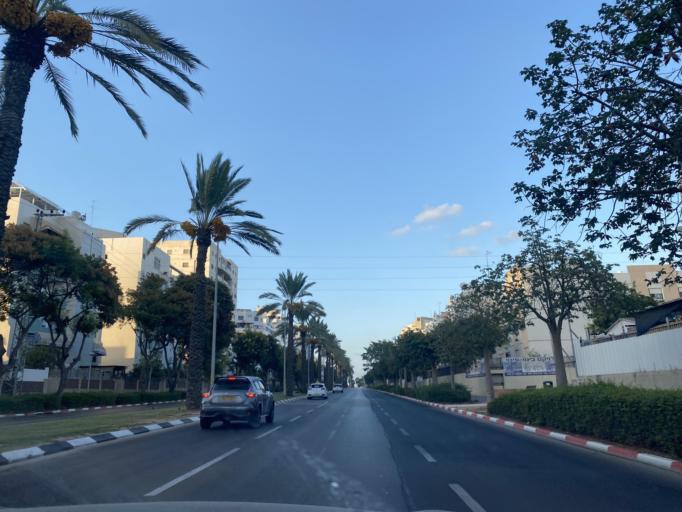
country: IL
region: Southern District
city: Ashdod
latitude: 31.7833
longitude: 34.6443
